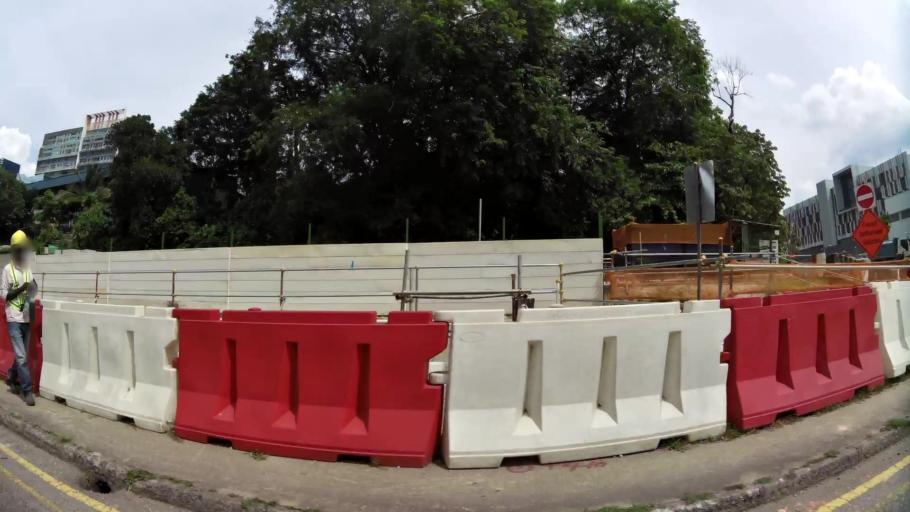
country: MY
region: Johor
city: Johor Bahru
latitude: 1.4050
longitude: 103.7563
